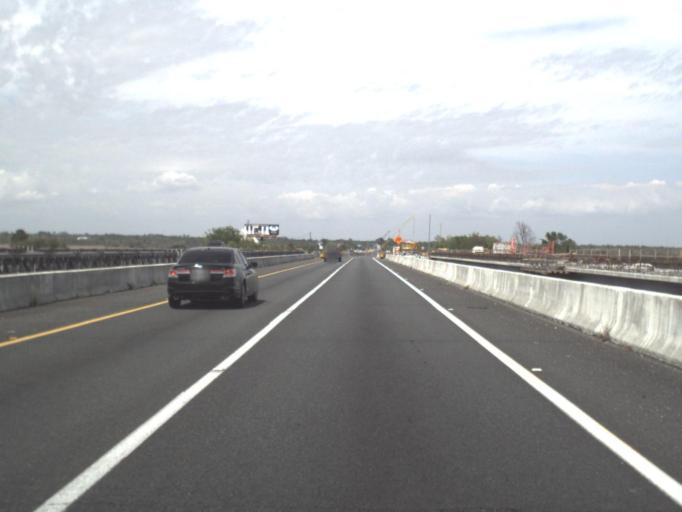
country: US
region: Florida
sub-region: Santa Rosa County
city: Pace
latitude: 30.5718
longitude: -87.1847
